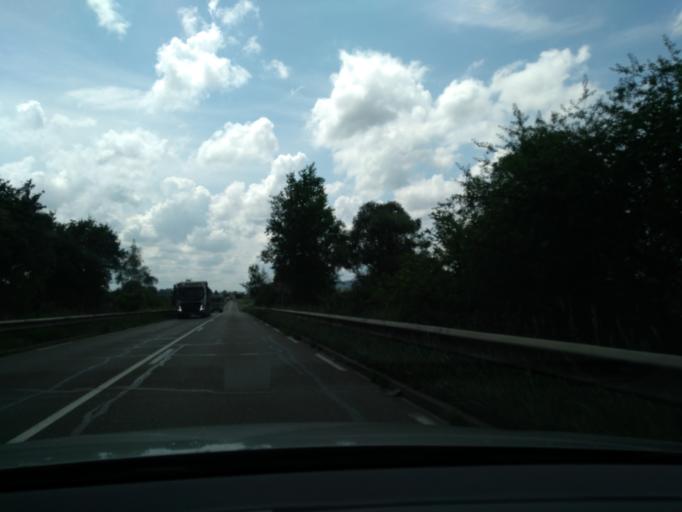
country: FR
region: Picardie
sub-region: Departement de l'Aisne
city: Athies-sous-Laon
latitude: 49.6015
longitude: 3.6625
